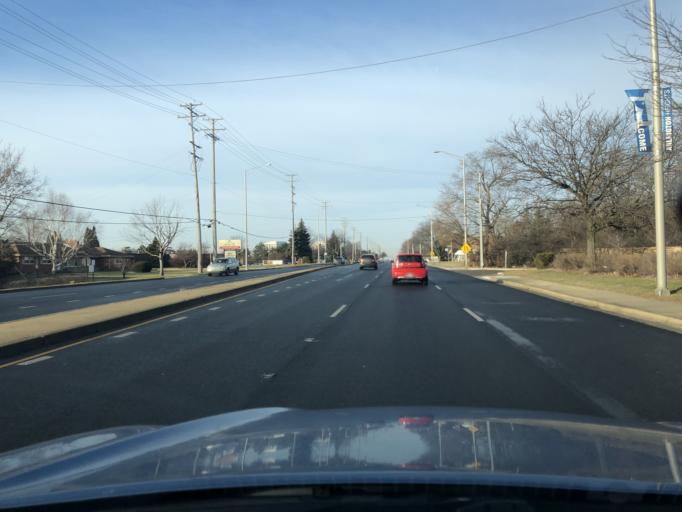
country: US
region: Illinois
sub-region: Cook County
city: Arlington Heights
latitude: 42.0515
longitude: -87.9850
